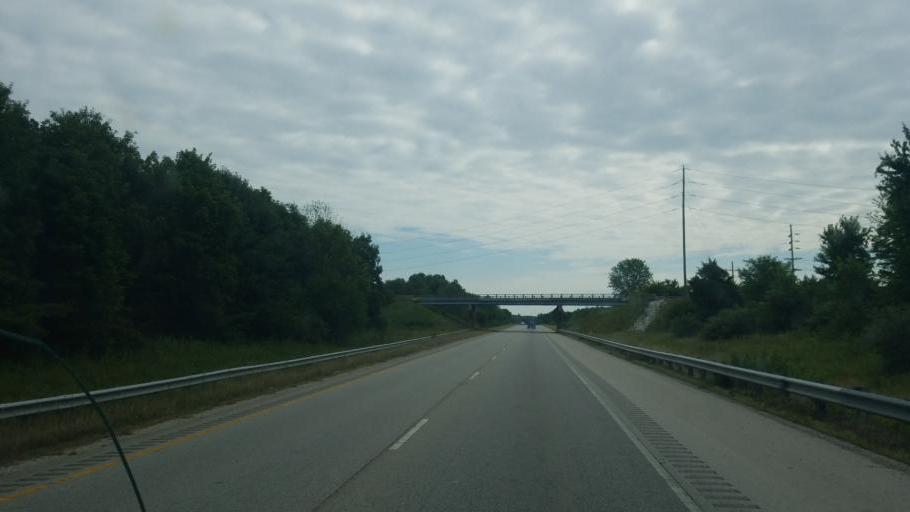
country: US
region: Indiana
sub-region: Vigo County
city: Seelyville
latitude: 39.4312
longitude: -87.2970
